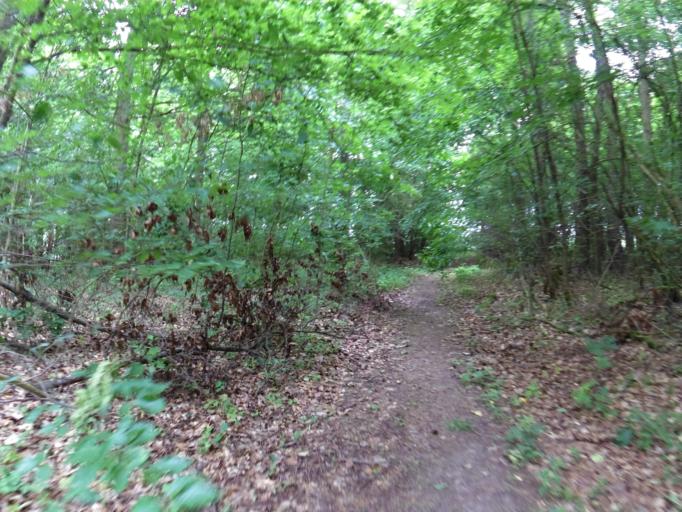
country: DE
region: Bavaria
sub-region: Regierungsbezirk Unterfranken
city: Zell am Main
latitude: 49.8182
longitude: 9.8506
